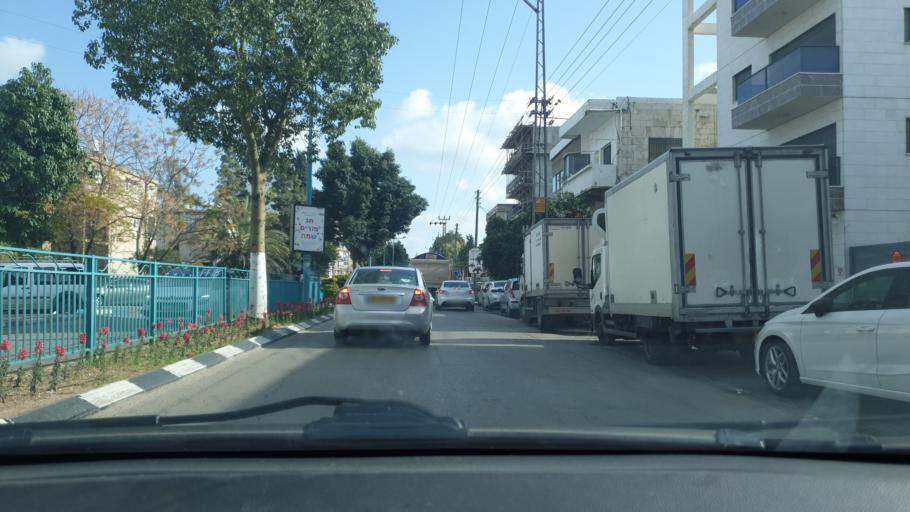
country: IL
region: Central District
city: Ramla
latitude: 31.9336
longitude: 34.8680
